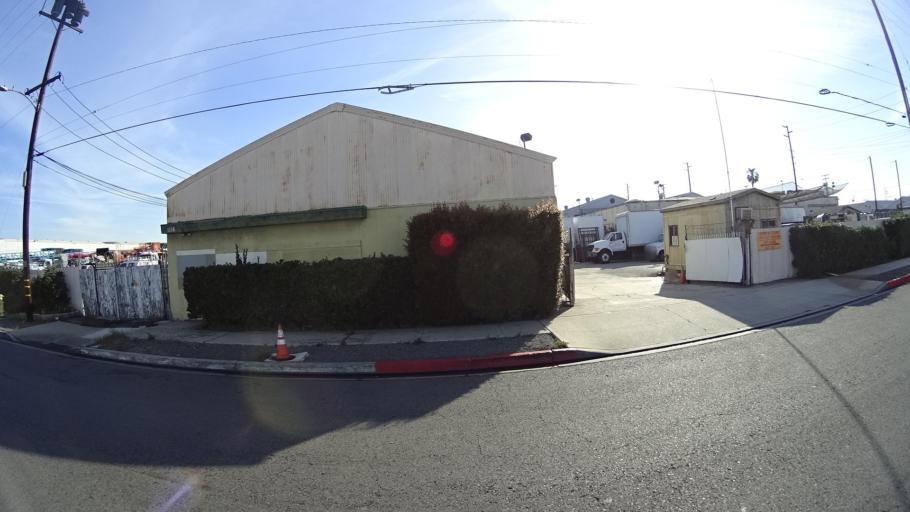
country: US
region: California
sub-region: Orange County
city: Anaheim
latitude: 33.8497
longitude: -117.9138
